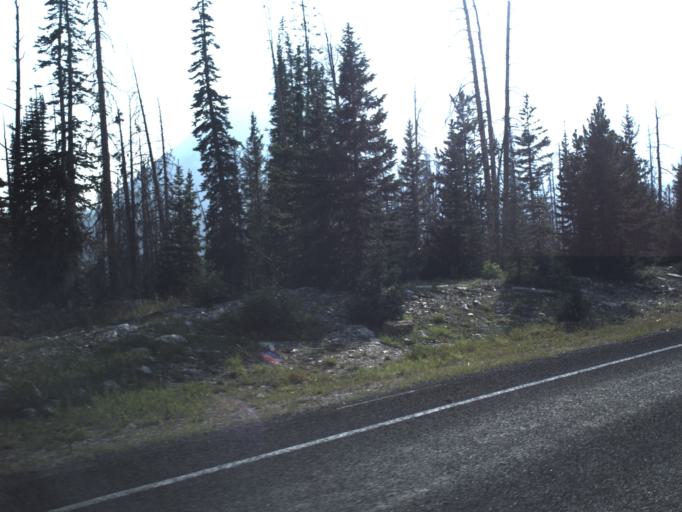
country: US
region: Utah
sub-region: Summit County
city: Kamas
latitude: 40.7119
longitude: -110.8821
